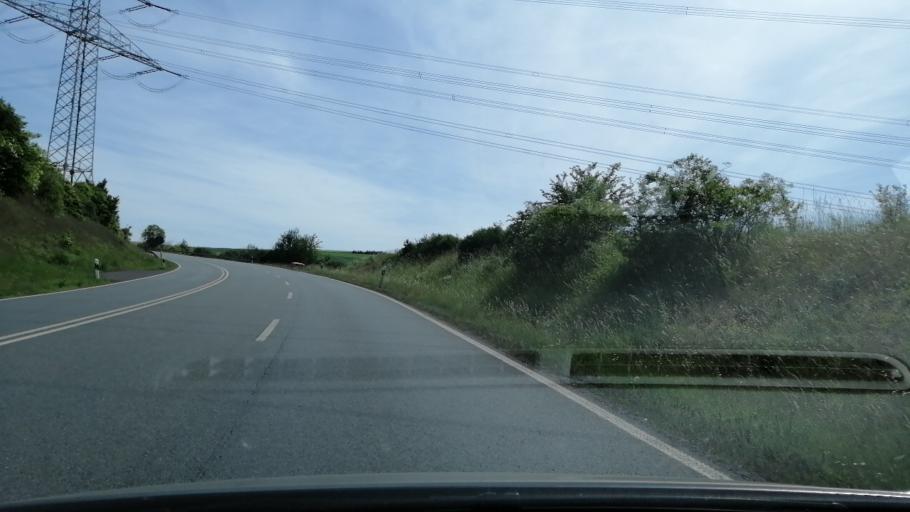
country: DE
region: Hesse
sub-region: Regierungsbezirk Kassel
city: Bad Wildungen
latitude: 51.1489
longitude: 9.1169
